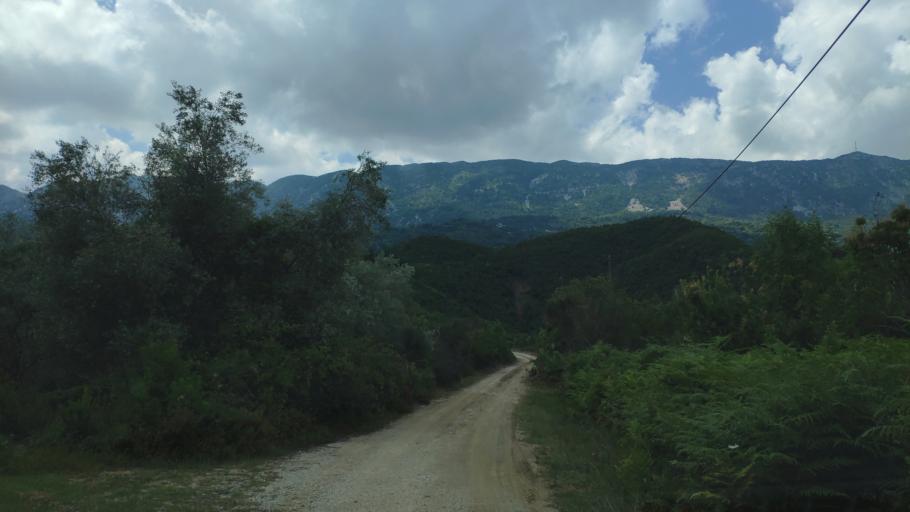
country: GR
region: Epirus
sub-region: Nomos Artas
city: Agios Dimitrios
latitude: 39.3158
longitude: 21.0163
